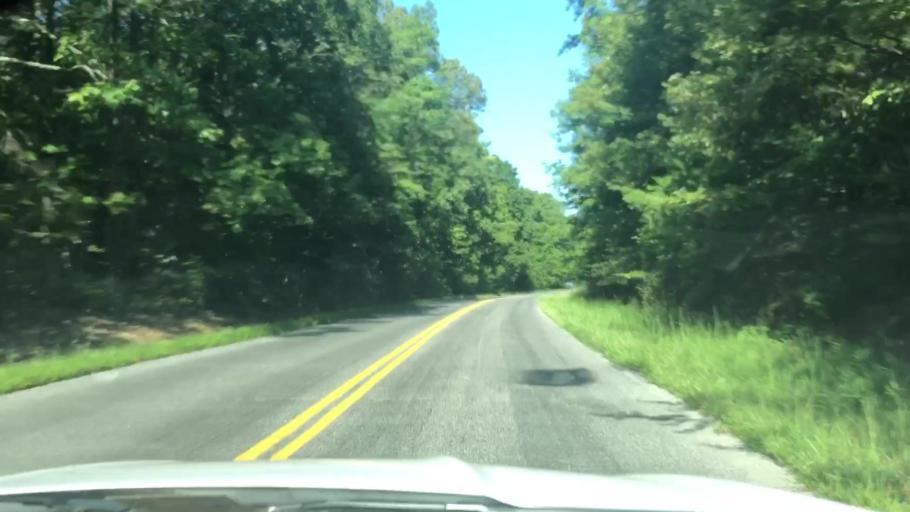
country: US
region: Virginia
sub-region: New Kent County
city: New Kent
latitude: 37.4838
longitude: -76.9271
